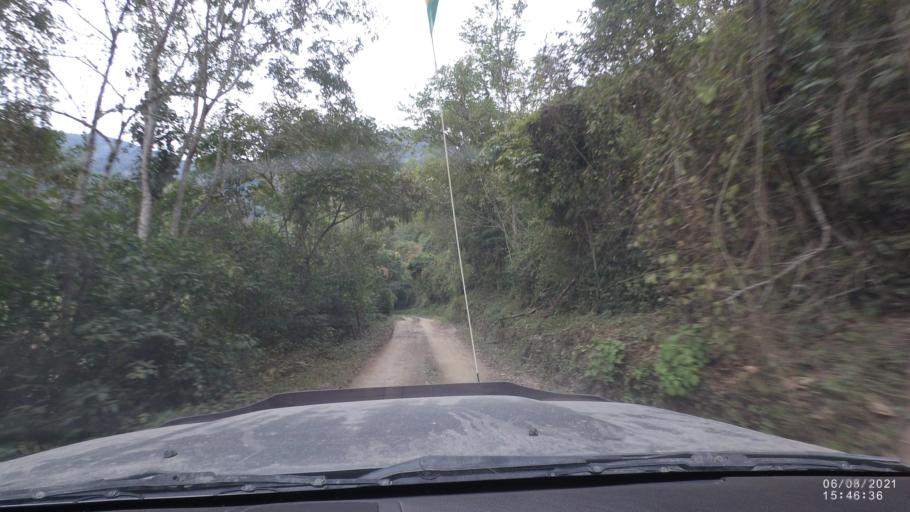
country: BO
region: La Paz
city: Quime
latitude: -16.5947
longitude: -66.7079
